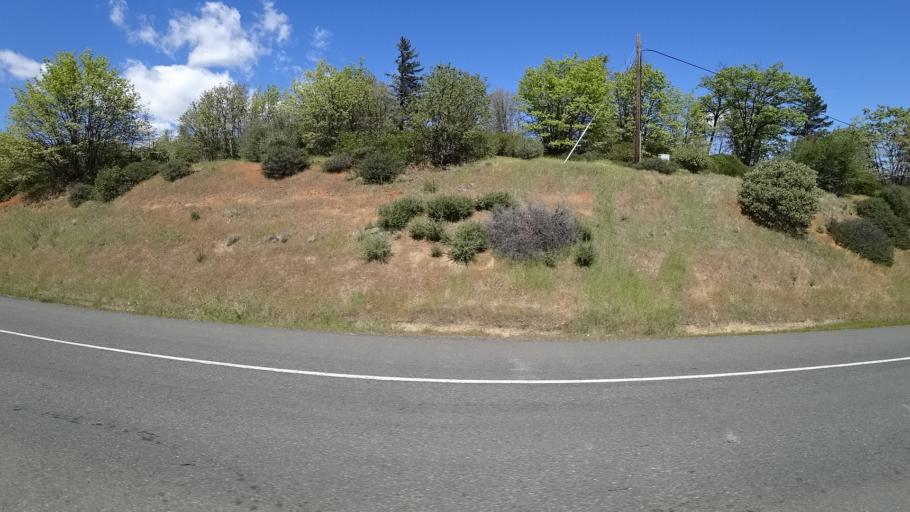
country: US
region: California
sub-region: Trinity County
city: Weaverville
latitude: 40.7360
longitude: -122.9634
